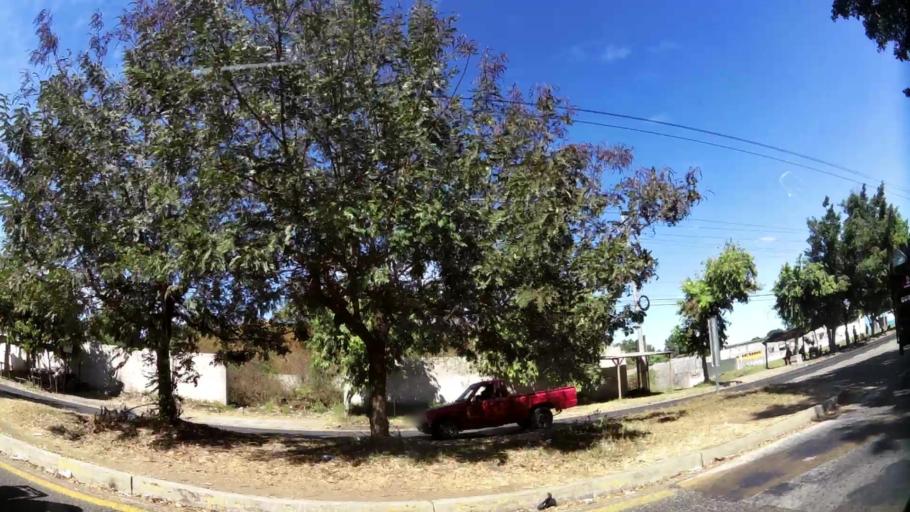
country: SV
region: Santa Ana
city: Chalchuapa
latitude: 13.9887
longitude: -89.6780
